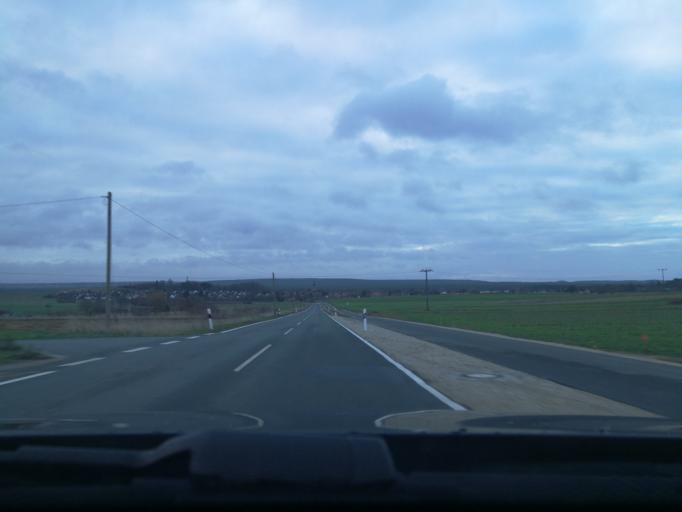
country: DE
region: Bavaria
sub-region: Regierungsbezirk Mittelfranken
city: Uttenreuth
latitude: 49.6092
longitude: 11.0731
